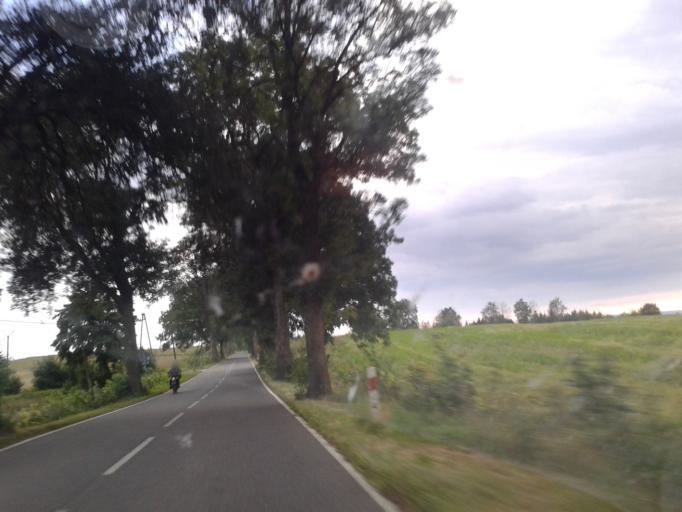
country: PL
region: West Pomeranian Voivodeship
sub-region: Powiat szczecinecki
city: Grzmiaca
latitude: 53.8785
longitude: 16.4970
